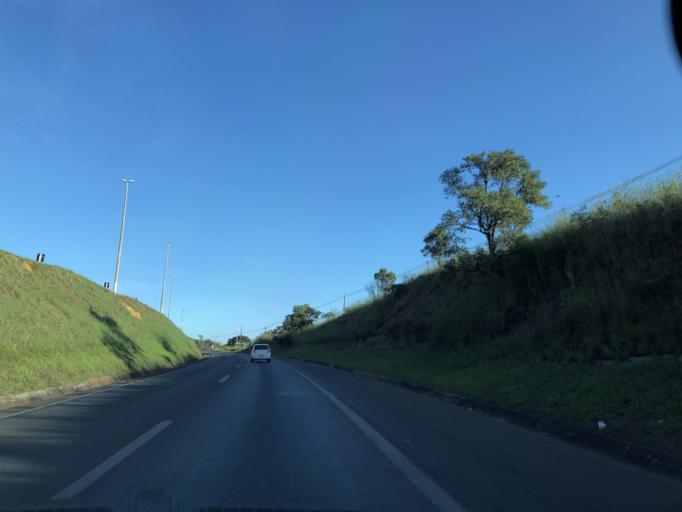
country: BR
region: Goias
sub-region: Luziania
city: Luziania
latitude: -16.1866
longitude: -47.9284
